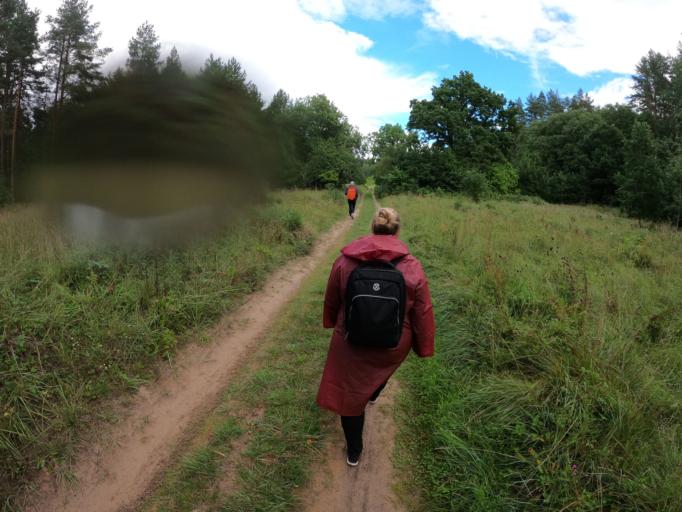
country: LV
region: Talsu Rajons
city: Stende
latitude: 57.0782
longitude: 22.4908
